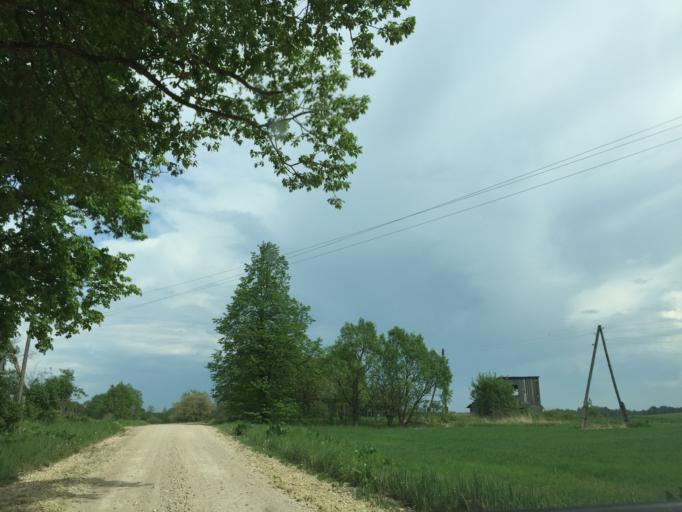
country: LV
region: Livani
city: Livani
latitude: 56.5839
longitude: 26.1853
